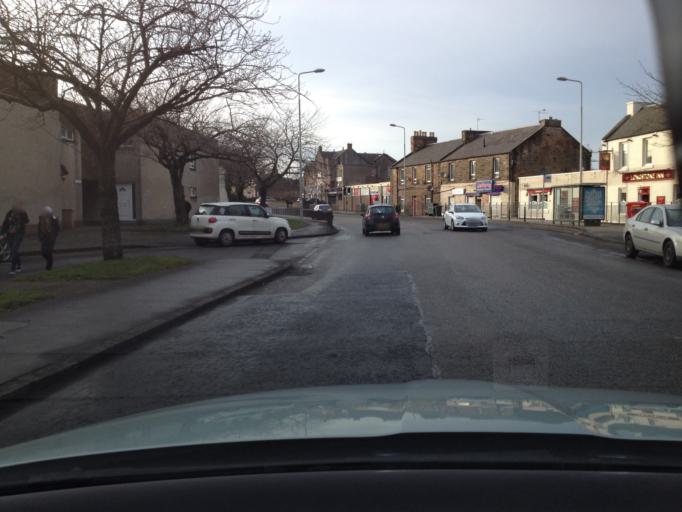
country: GB
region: Scotland
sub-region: Edinburgh
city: Colinton
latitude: 55.9253
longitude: -3.2583
